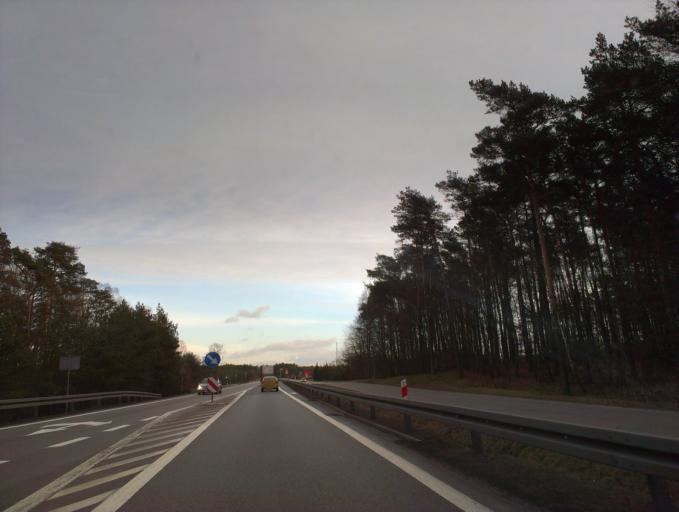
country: PL
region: Kujawsko-Pomorskie
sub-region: Powiat lipnowski
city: Skepe
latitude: 52.8770
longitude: 19.3411
